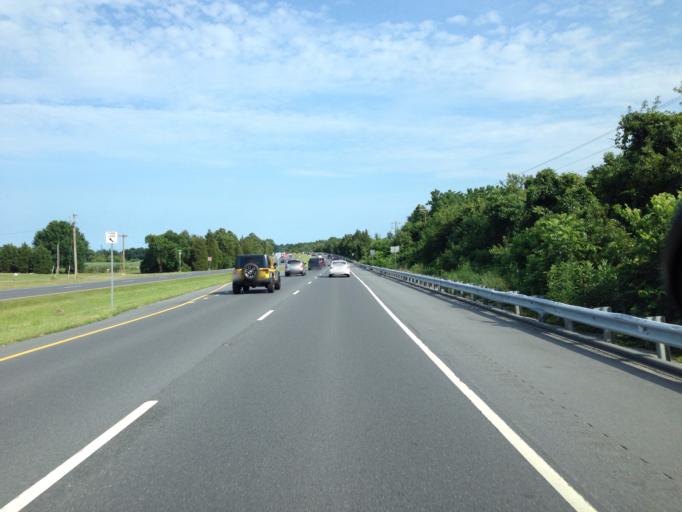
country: US
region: Delaware
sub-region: Sussex County
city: Milton
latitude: 38.7943
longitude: -75.2567
